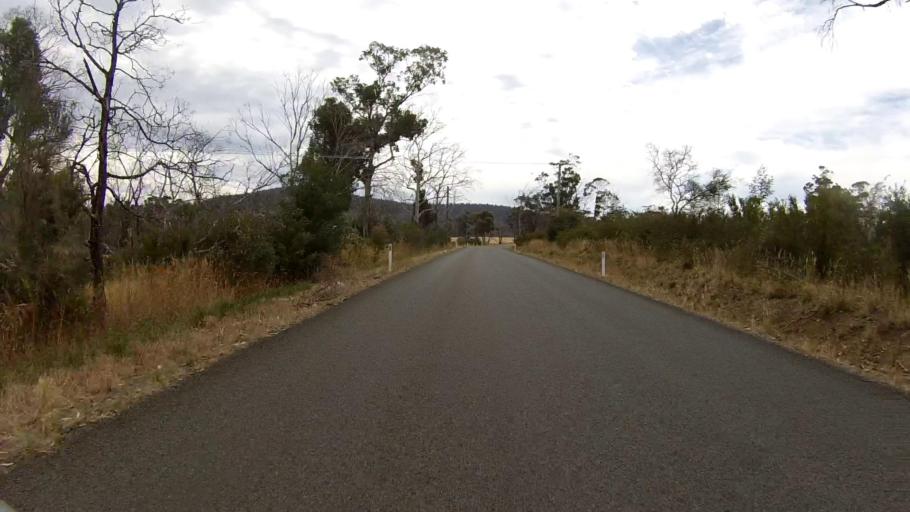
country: AU
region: Tasmania
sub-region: Sorell
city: Sorell
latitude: -42.8934
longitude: 147.7798
